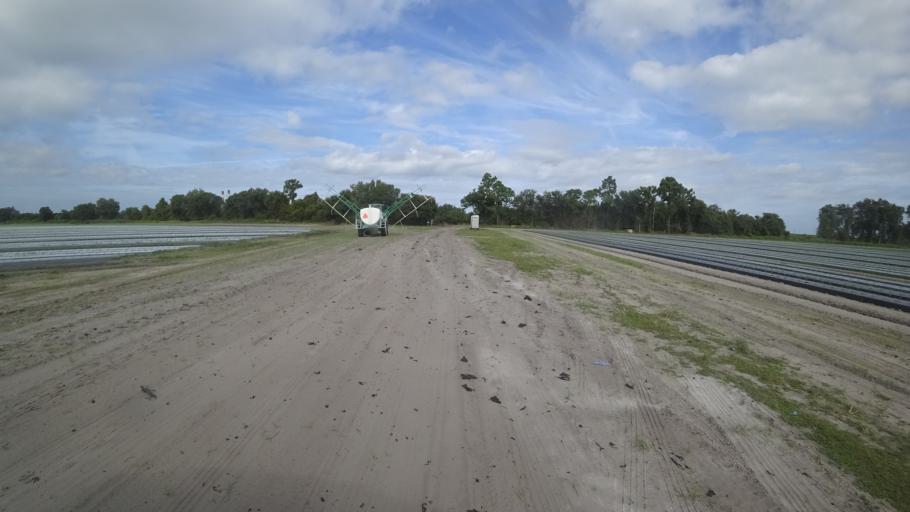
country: US
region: Florida
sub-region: Hillsborough County
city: Wimauma
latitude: 27.5995
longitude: -82.3253
